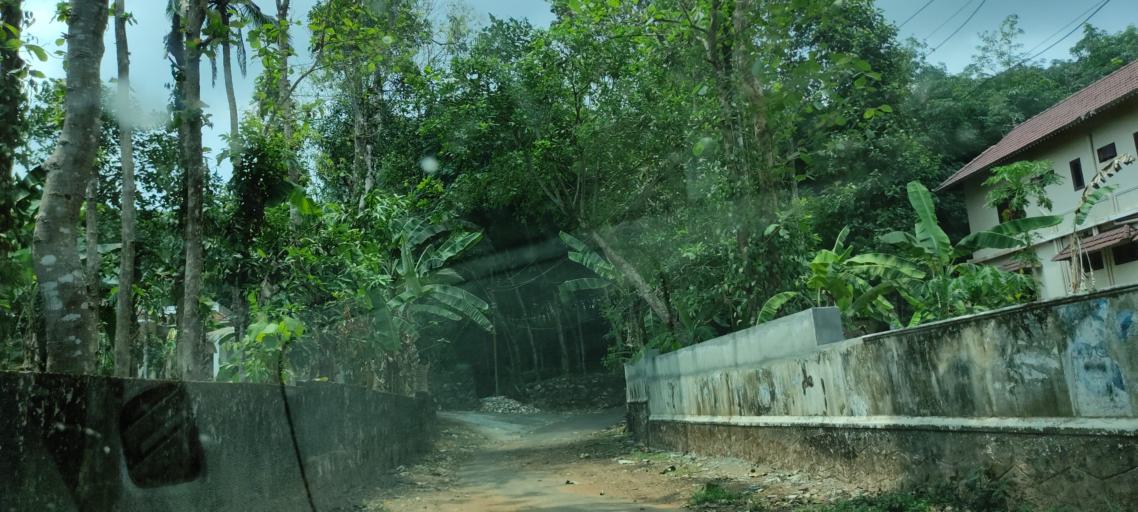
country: IN
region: Kerala
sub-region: Pattanamtitta
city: Adur
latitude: 9.1712
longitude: 76.7469
